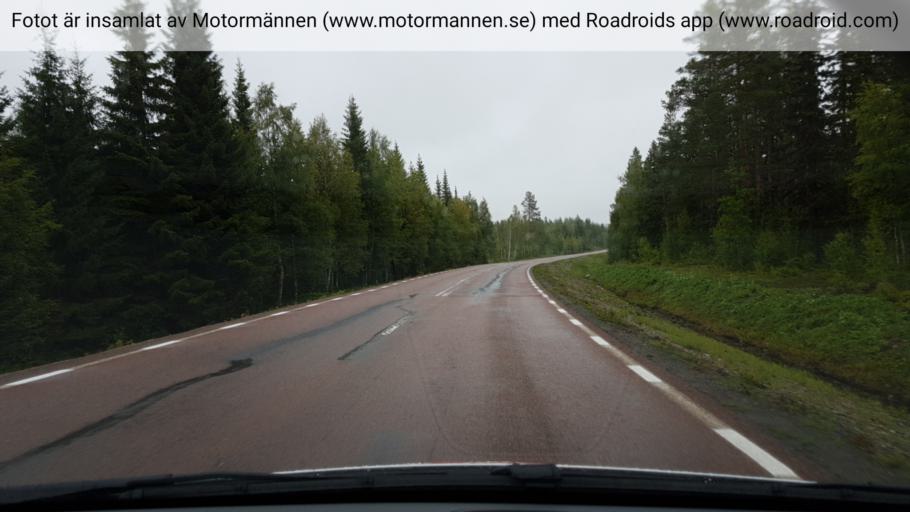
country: SE
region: Jaemtland
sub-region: Stroemsunds Kommun
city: Stroemsund
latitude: 63.8884
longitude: 15.6864
